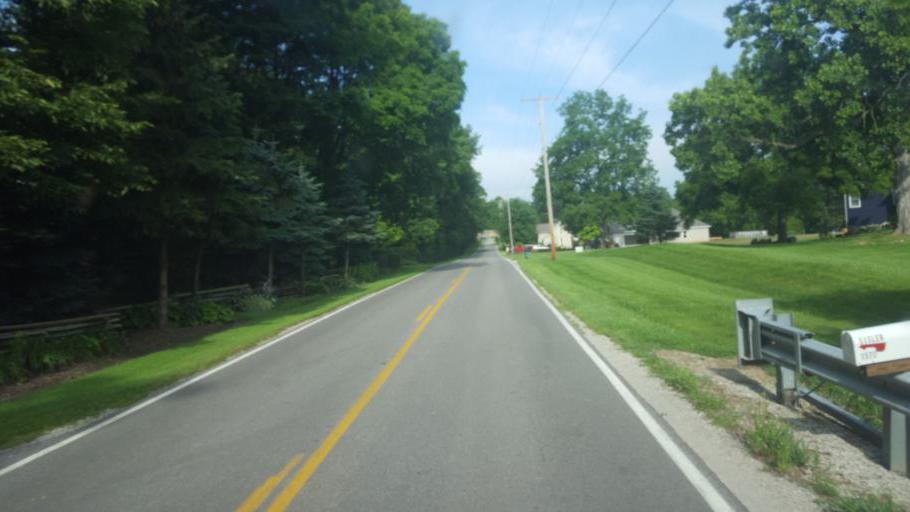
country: US
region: Ohio
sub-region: Marion County
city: Marion
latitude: 40.5202
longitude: -83.1543
